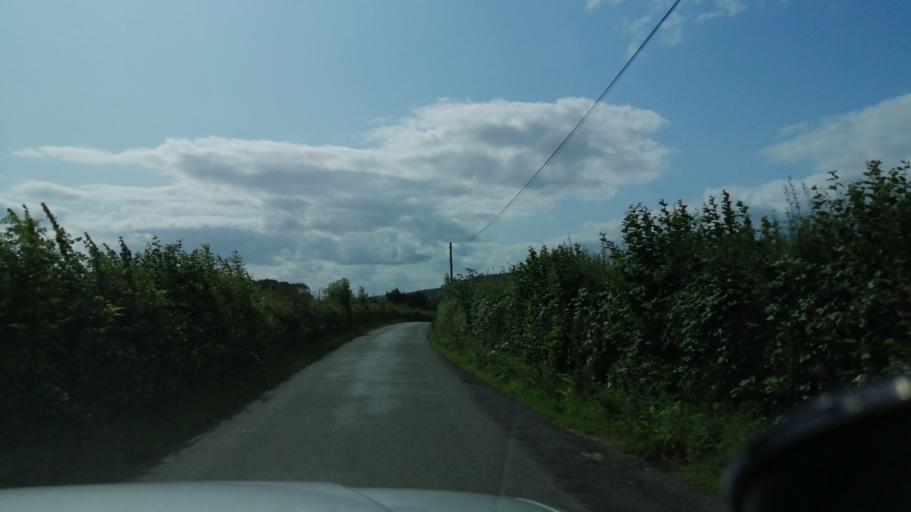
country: GB
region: England
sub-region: Herefordshire
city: Kinnersley
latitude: 52.1313
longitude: -2.9627
